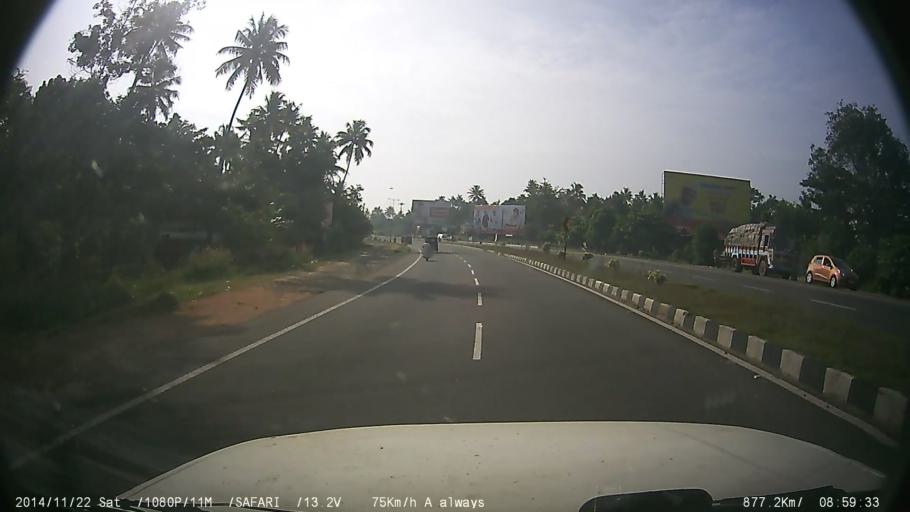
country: IN
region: Kerala
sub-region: Thrissur District
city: Irinjalakuda
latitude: 10.3886
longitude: 76.2885
